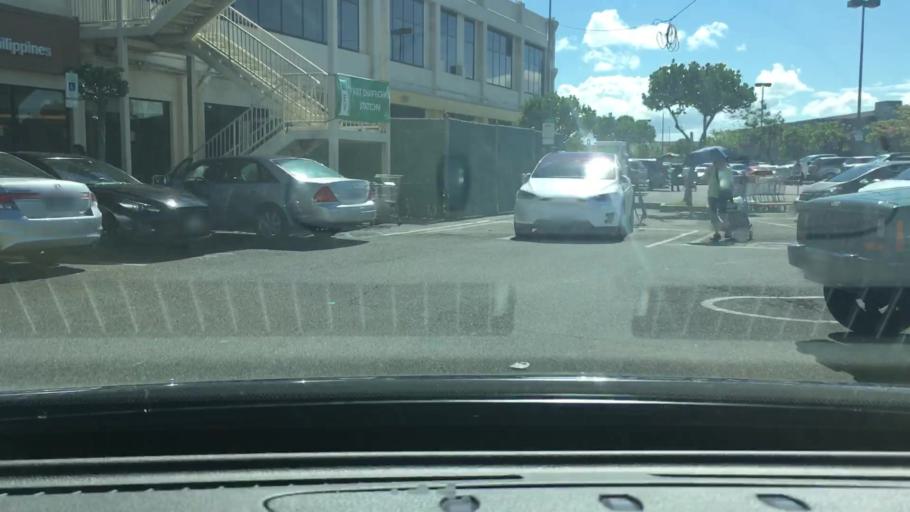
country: US
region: Hawaii
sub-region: Honolulu County
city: Honolulu
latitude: 21.3183
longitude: -157.8694
